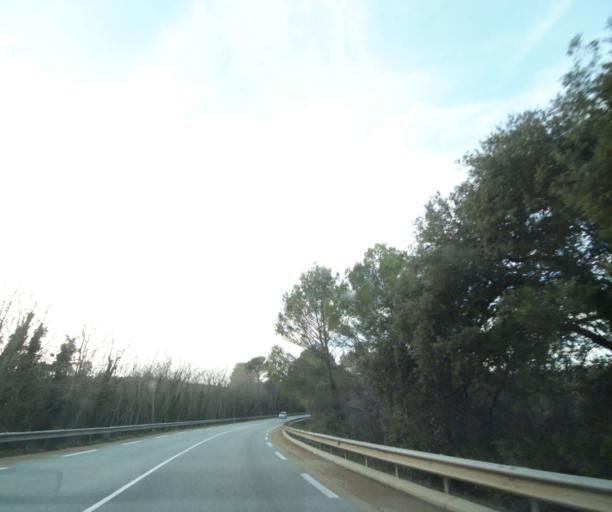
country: FR
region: Provence-Alpes-Cote d'Azur
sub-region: Departement du Var
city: La Motte
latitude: 43.4819
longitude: 6.5150
